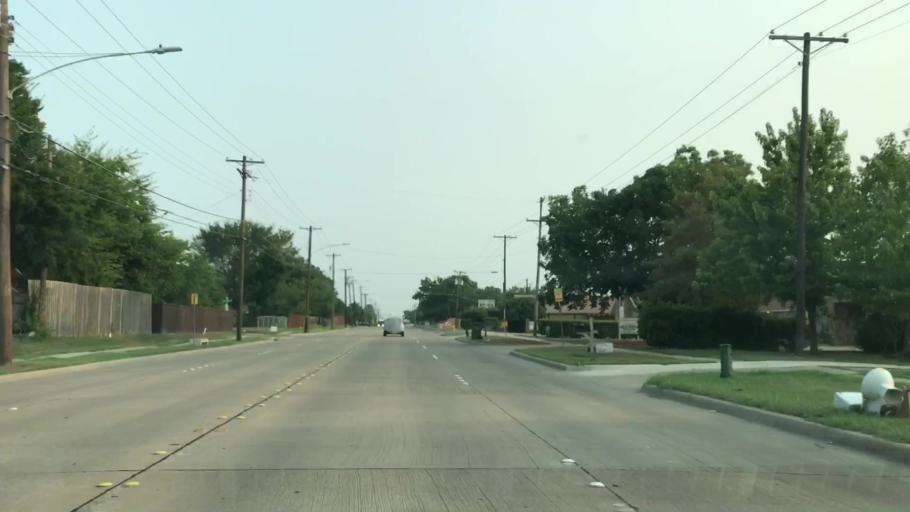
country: US
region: Texas
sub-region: Dallas County
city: Garland
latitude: 32.9008
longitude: -96.6222
